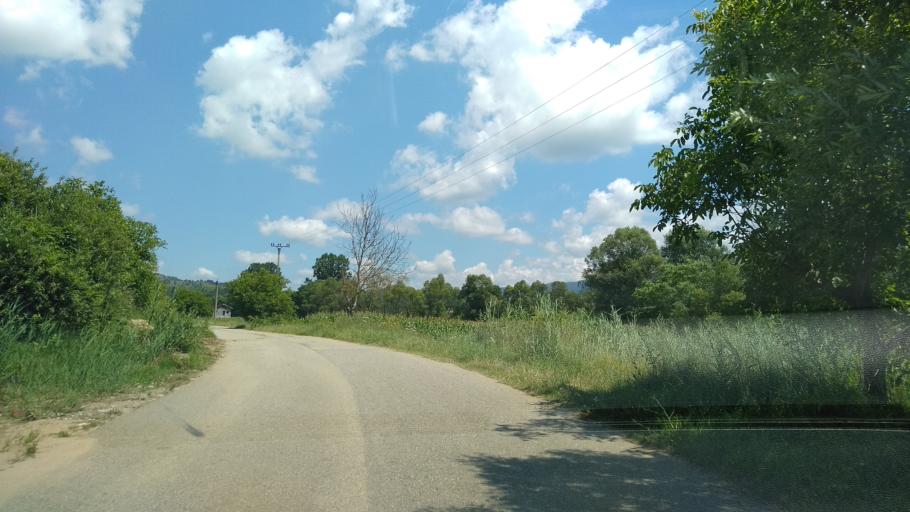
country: RO
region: Hunedoara
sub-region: Comuna Bosorod
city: Bosorod
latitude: 45.7064
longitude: 23.1067
